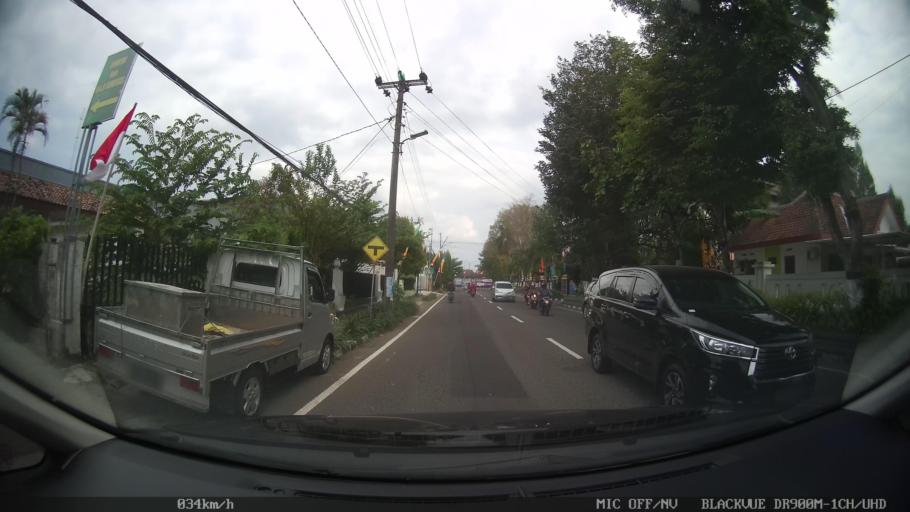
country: ID
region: Daerah Istimewa Yogyakarta
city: Yogyakarta
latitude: -7.8004
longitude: 110.3846
